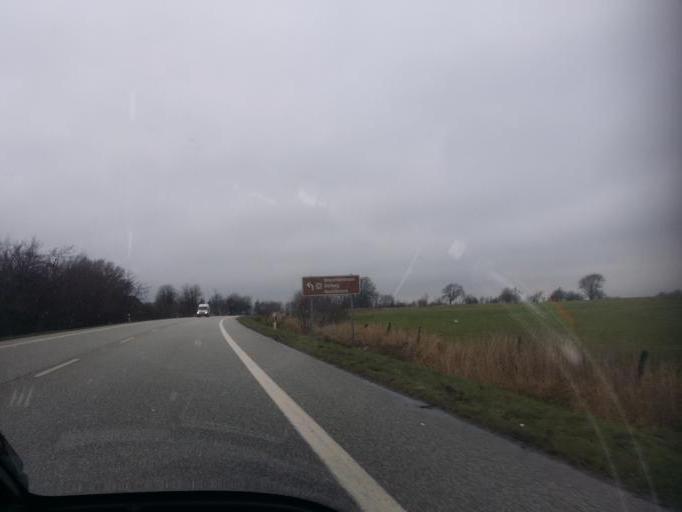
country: DE
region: Schleswig-Holstein
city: Bordelum
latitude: 54.6430
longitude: 8.9469
